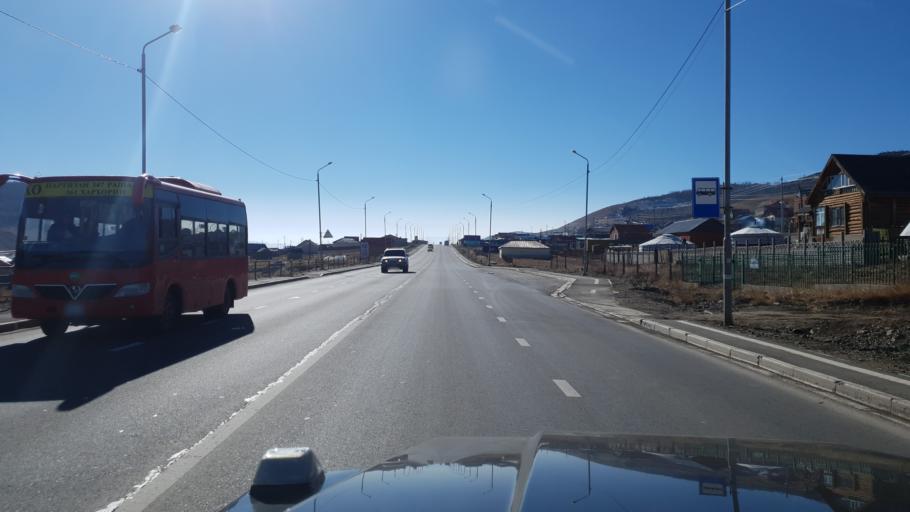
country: MN
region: Ulaanbaatar
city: Ulaanbaatar
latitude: 48.0435
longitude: 106.9030
